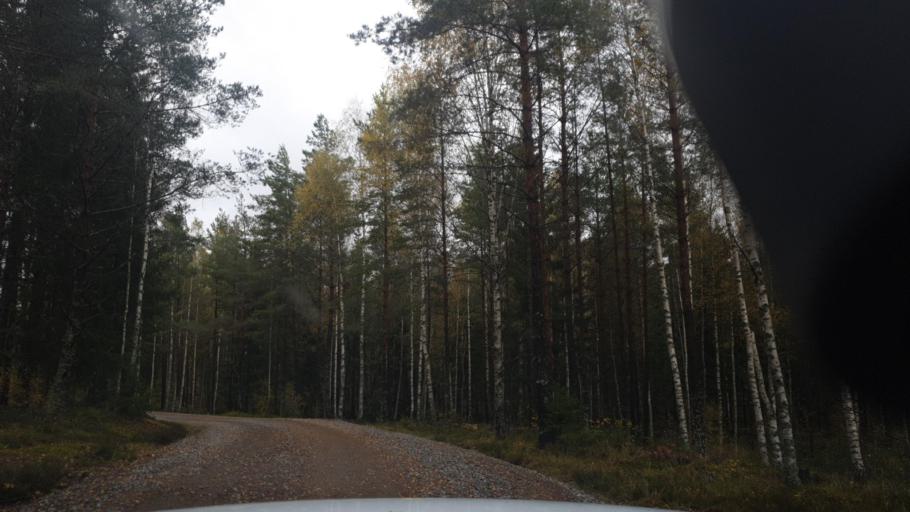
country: SE
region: Vaermland
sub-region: Karlstads Kommun
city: Edsvalla
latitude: 59.4588
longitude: 13.0991
